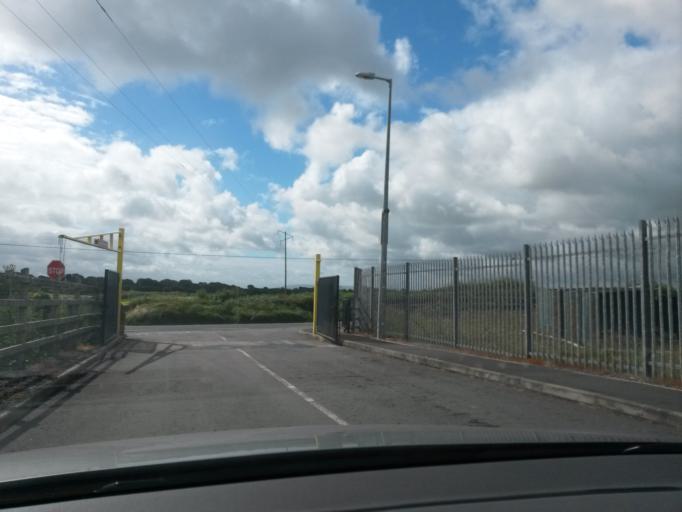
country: IE
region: Connaught
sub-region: County Galway
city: Gort
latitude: 53.1554
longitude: -8.8168
